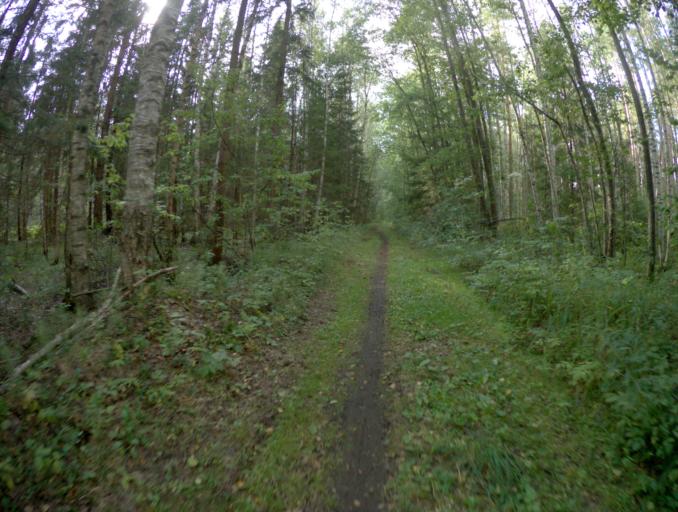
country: RU
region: Vladimir
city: Sobinka
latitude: 55.9148
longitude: 40.0981
